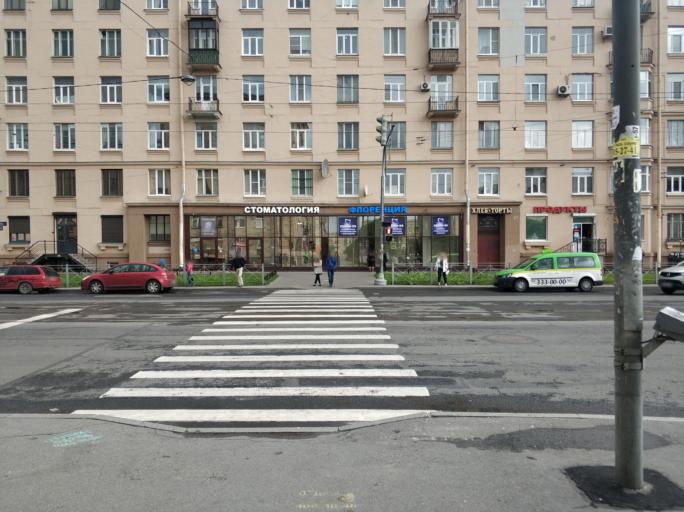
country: RU
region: St.-Petersburg
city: Kupchino
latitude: 59.8536
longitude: 30.3294
